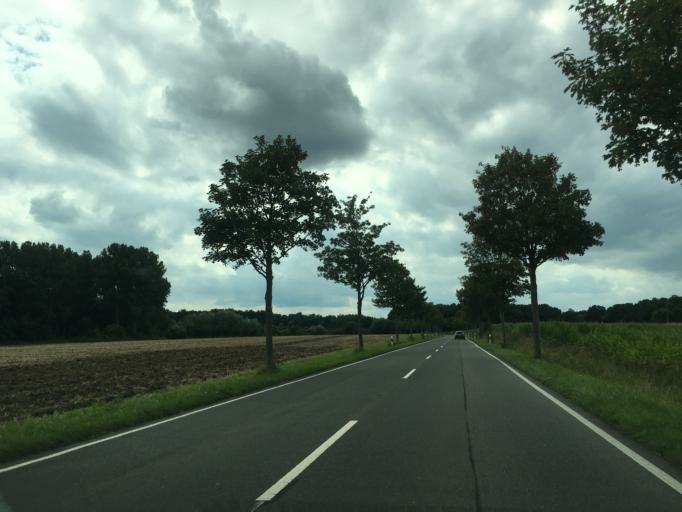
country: DE
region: North Rhine-Westphalia
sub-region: Regierungsbezirk Munster
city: Nordkirchen
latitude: 51.7680
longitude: 7.5394
